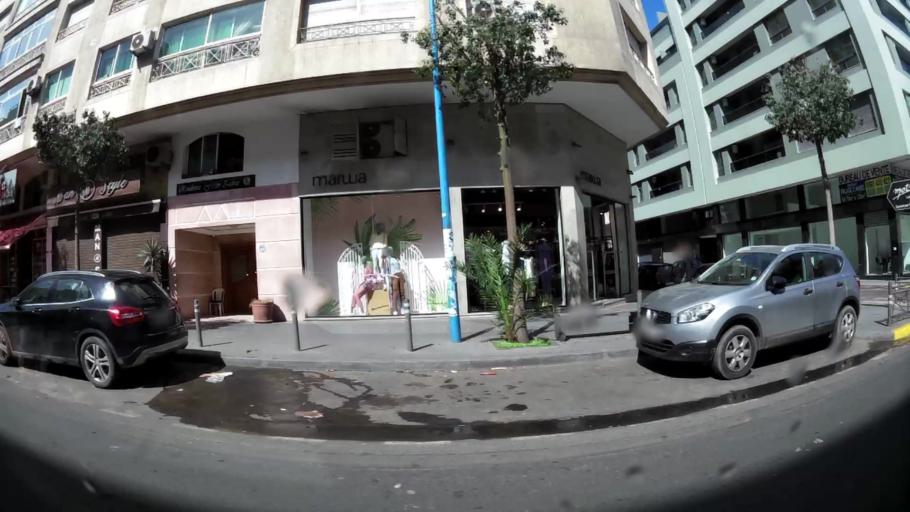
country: MA
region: Grand Casablanca
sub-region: Casablanca
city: Casablanca
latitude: 33.5800
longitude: -7.6151
